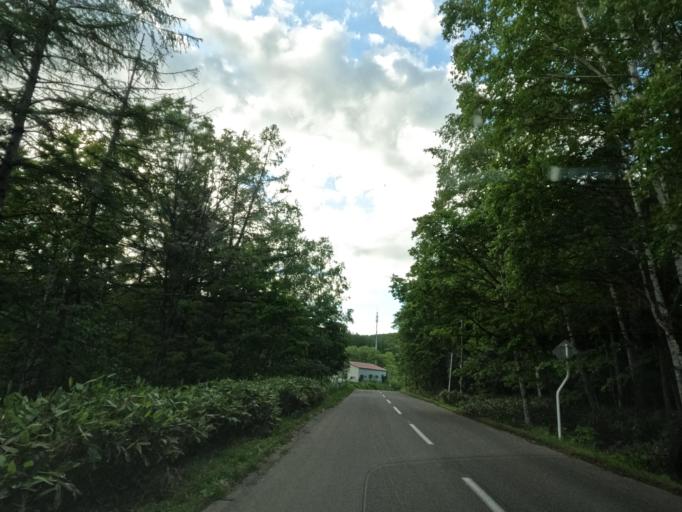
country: JP
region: Hokkaido
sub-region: Asahikawa-shi
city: Asahikawa
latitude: 43.8799
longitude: 142.4548
